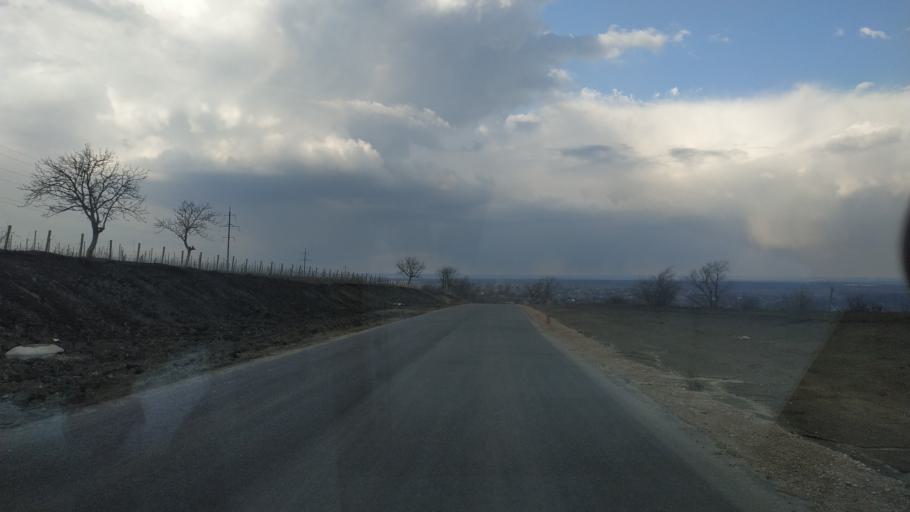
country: MD
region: Anenii Noi
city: Anenii Noi
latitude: 46.9945
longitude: 29.2838
